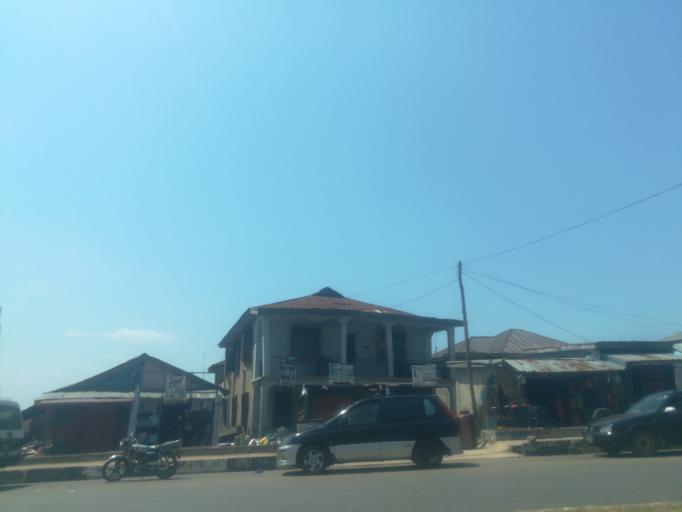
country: NG
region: Ogun
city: Abeokuta
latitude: 7.1574
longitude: 3.3493
